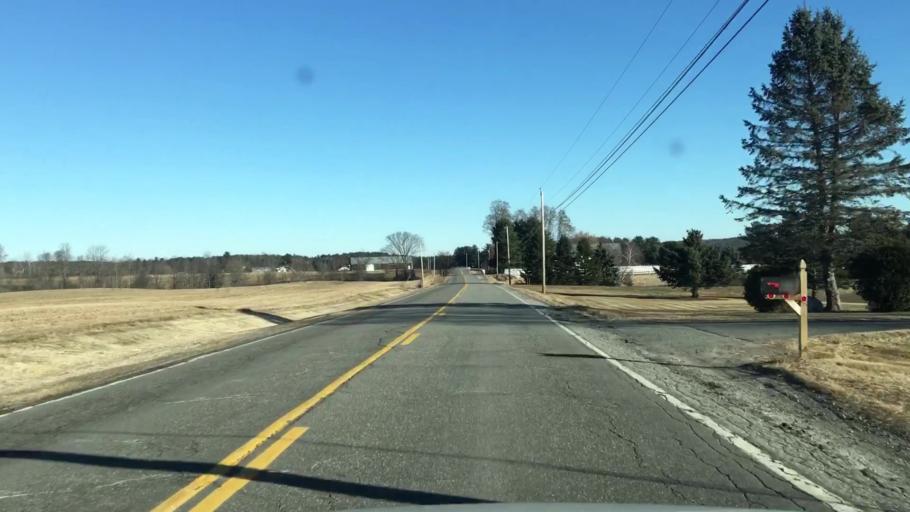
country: US
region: Maine
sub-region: Somerset County
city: Fairfield
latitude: 44.5566
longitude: -69.5836
